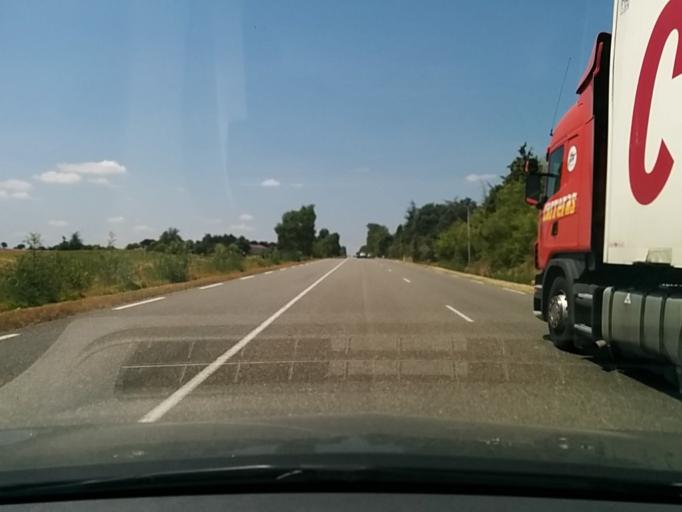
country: FR
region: Midi-Pyrenees
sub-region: Departement du Gers
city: Gimont
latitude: 43.6338
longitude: 0.8532
